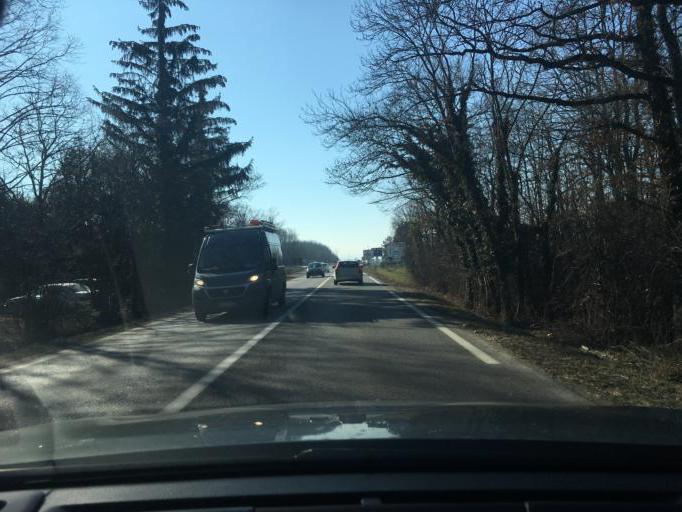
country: FR
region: Rhone-Alpes
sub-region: Departement de la Haute-Savoie
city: Cranves-Sales
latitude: 46.2043
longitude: 6.2856
